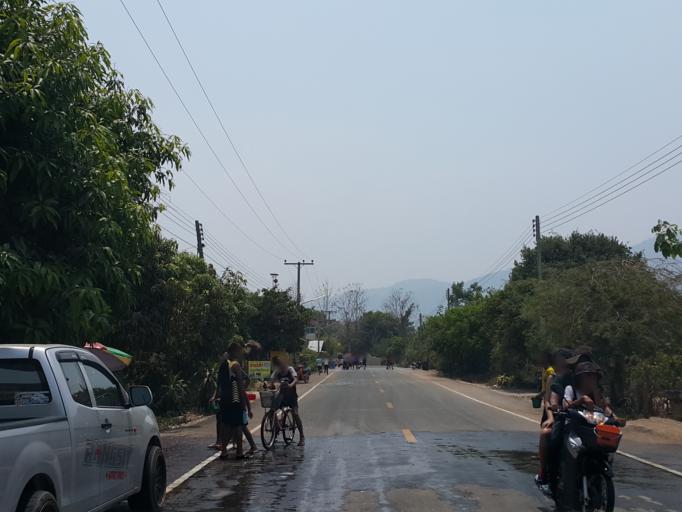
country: TH
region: Kamphaeng Phet
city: Pang Sila Thong
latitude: 15.9971
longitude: 99.3713
